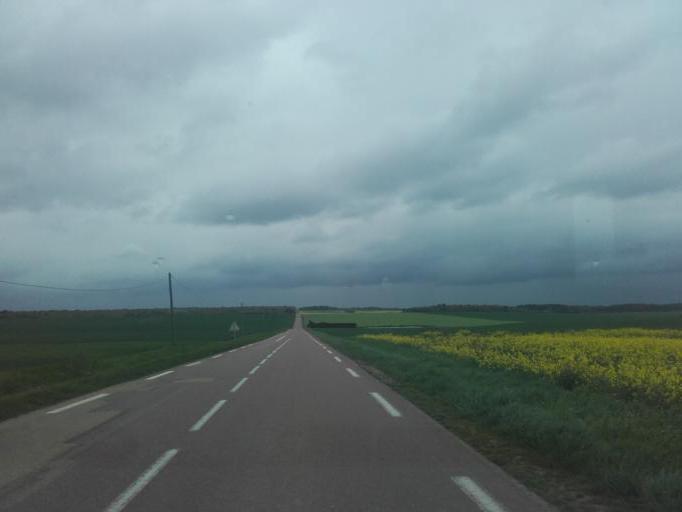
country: FR
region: Bourgogne
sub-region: Departement de l'Yonne
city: Joux-la-Ville
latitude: 47.6774
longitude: 3.8736
